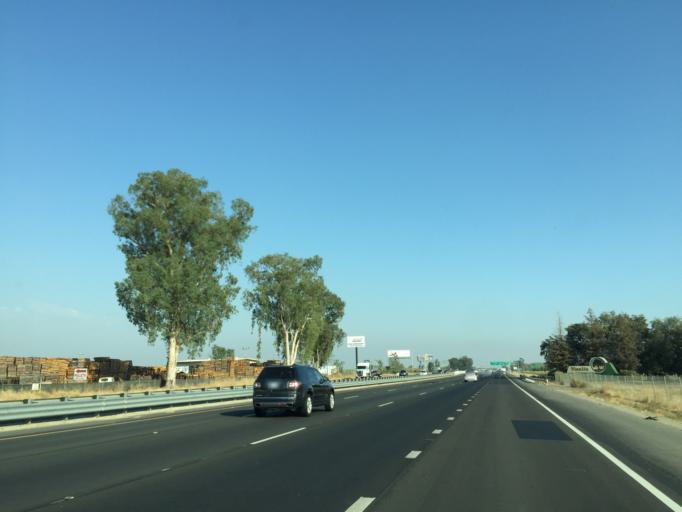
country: US
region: California
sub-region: Tulare County
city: Goshen
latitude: 36.3383
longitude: -119.4172
